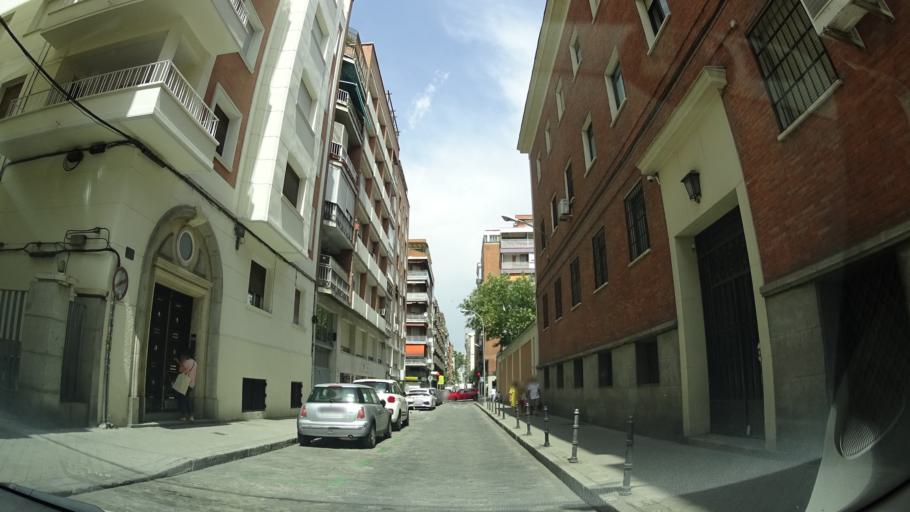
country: ES
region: Madrid
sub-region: Provincia de Madrid
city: Chamberi
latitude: 40.4276
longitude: -3.7163
